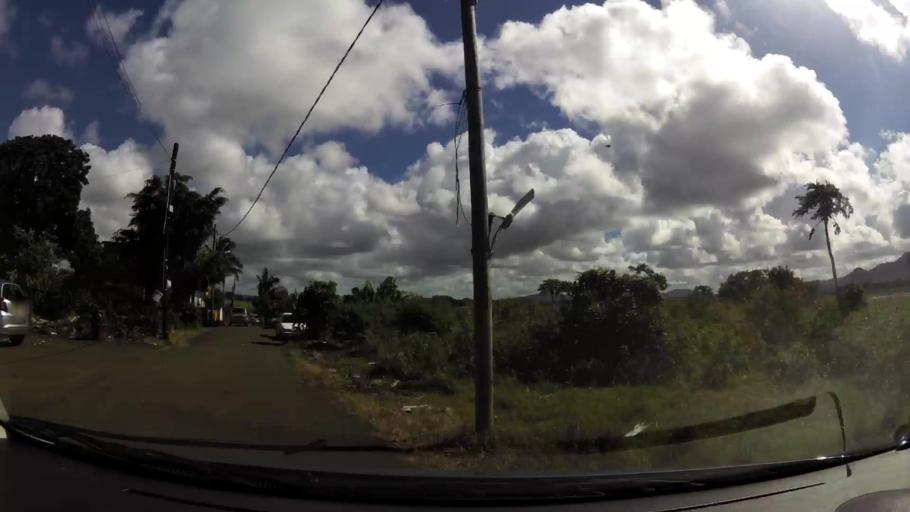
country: MU
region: Grand Port
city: Plaine Magnien
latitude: -20.4263
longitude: 57.6700
